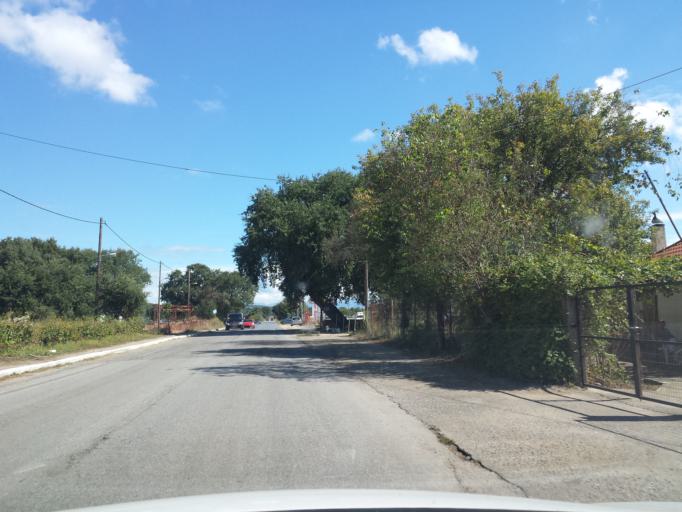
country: GR
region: Peloponnese
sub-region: Nomos Messinias
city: Vlakhopoulon
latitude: 36.9710
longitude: 21.8090
